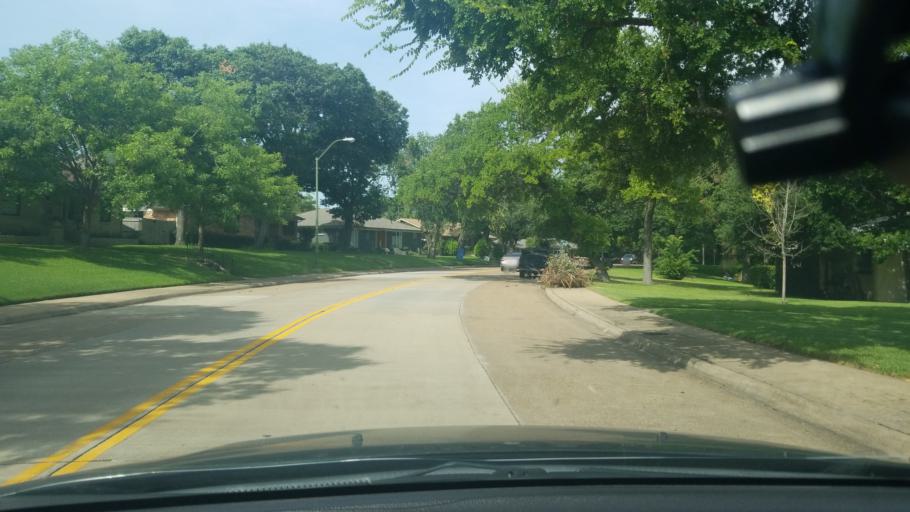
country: US
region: Texas
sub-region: Dallas County
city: Highland Park
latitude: 32.7997
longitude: -96.6967
